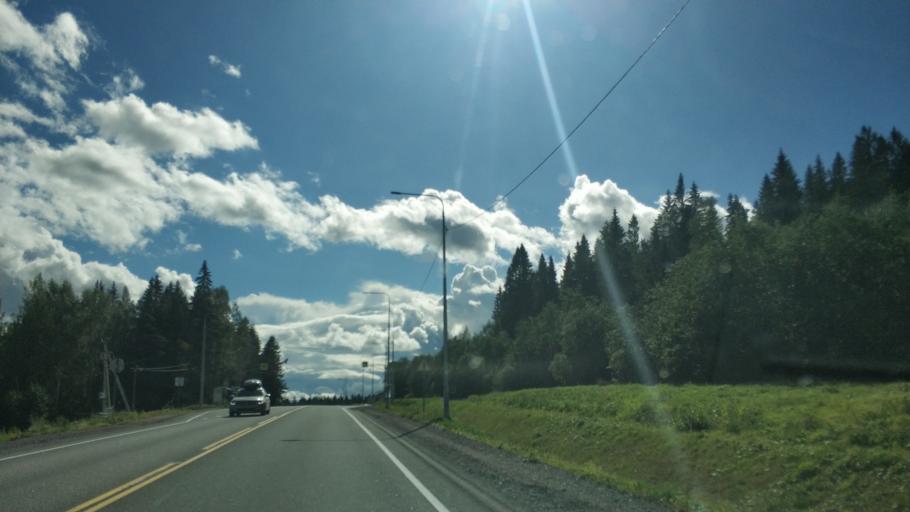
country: RU
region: Republic of Karelia
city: Ruskeala
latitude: 61.8856
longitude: 30.6441
